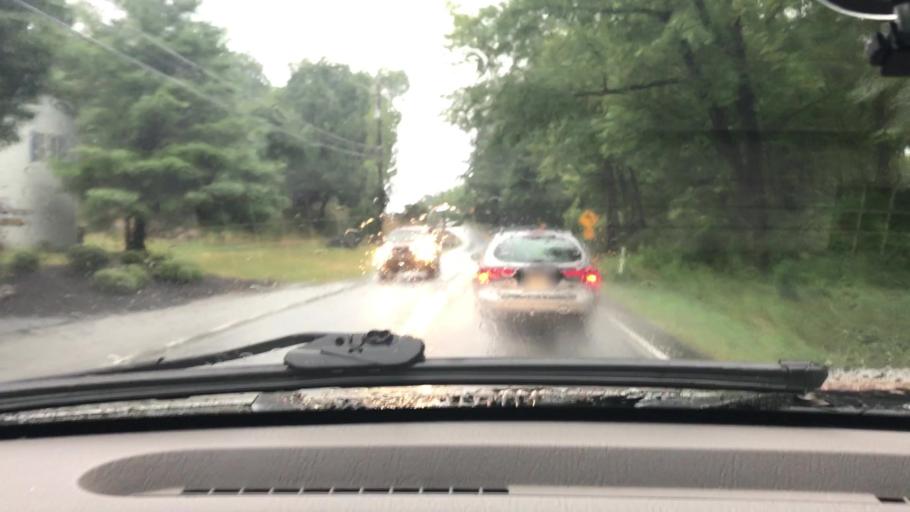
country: US
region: Pennsylvania
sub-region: Lancaster County
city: Elizabethtown
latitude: 40.1466
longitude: -76.6216
